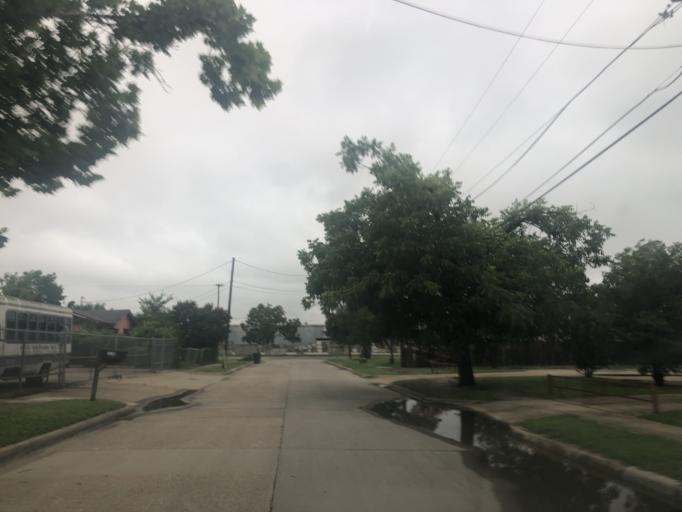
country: US
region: Texas
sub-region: Dallas County
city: Cockrell Hill
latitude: 32.7808
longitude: -96.8817
